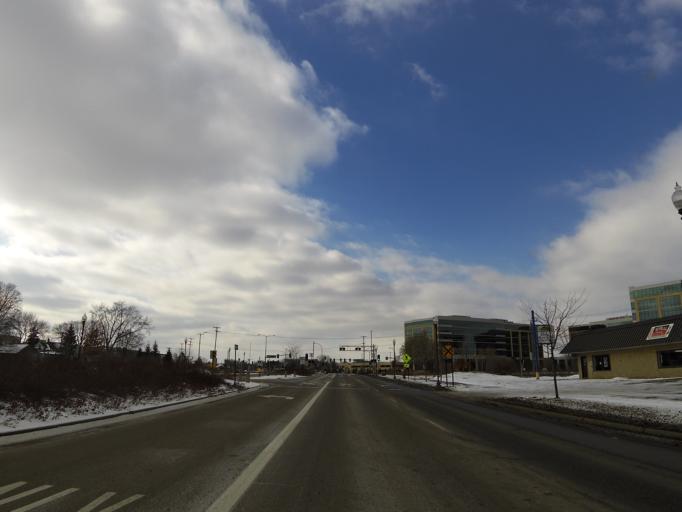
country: US
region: Minnesota
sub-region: Hennepin County
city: Minnetonka Mills
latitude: 44.9246
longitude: -93.3938
